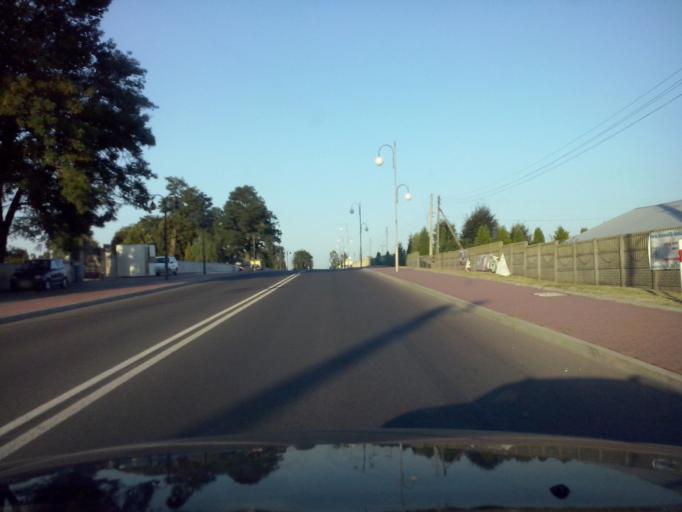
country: PL
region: Swietokrzyskie
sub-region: Powiat kielecki
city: Chmielnik
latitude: 50.6151
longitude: 20.7600
